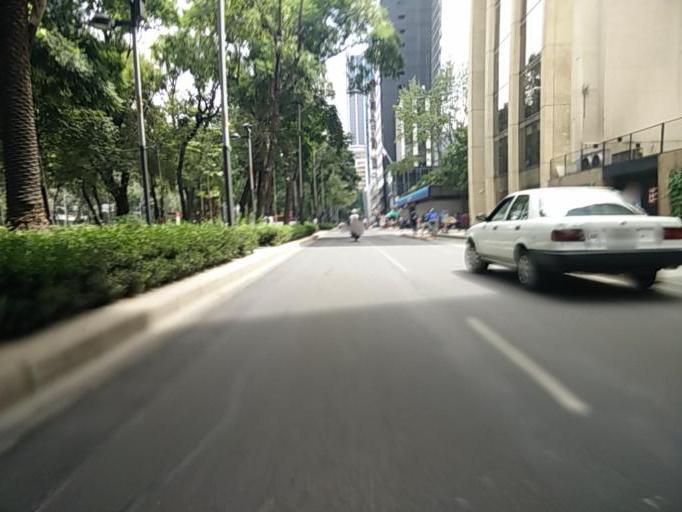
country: MX
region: Mexico City
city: Benito Juarez
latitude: 19.4251
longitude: -99.1705
